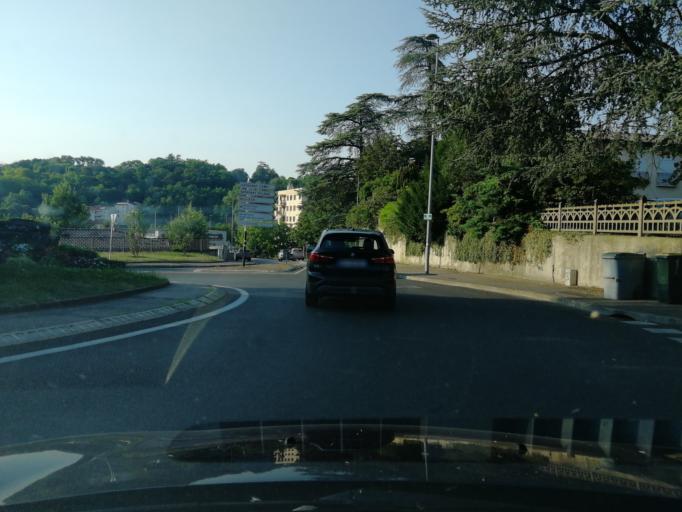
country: FR
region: Rhone-Alpes
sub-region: Departement du Rhone
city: Fontaines-sur-Saone
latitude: 45.8306
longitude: 4.8564
